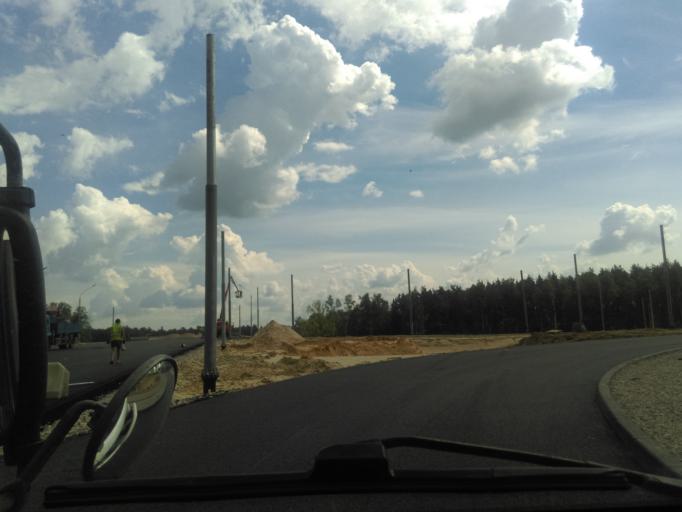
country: RU
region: Moskovskaya
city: Vostryakovo
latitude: 55.4329
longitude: 37.8694
